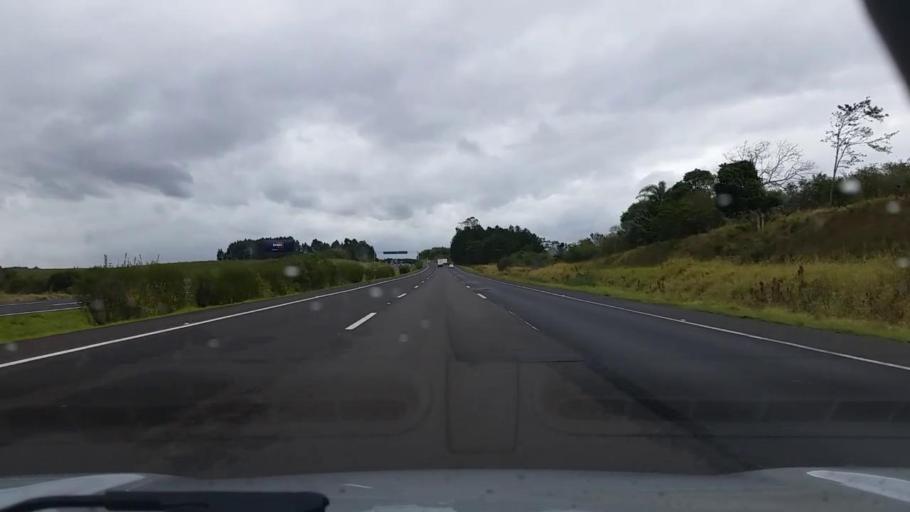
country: BR
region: Rio Grande do Sul
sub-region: Gravatai
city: Gravatai
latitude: -29.9225
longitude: -50.8488
